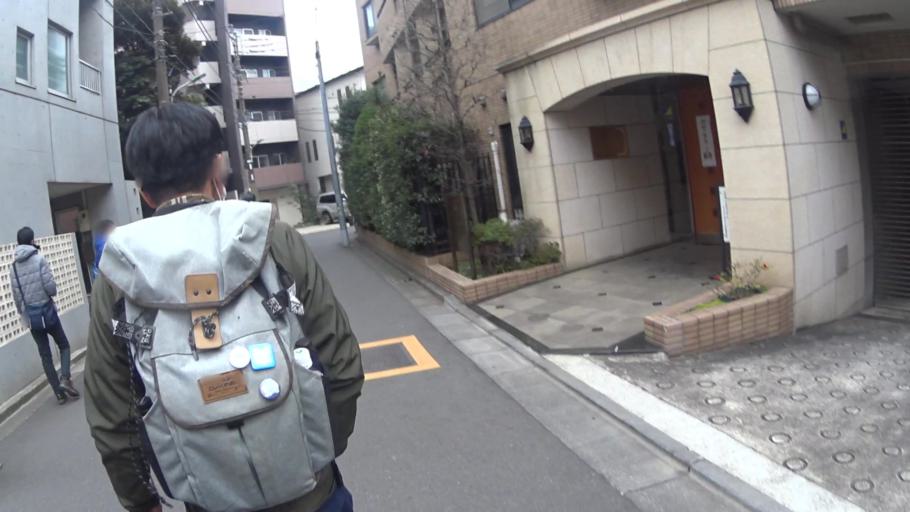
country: JP
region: Kanagawa
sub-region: Kawasaki-shi
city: Kawasaki
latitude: 35.5878
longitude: 139.7262
